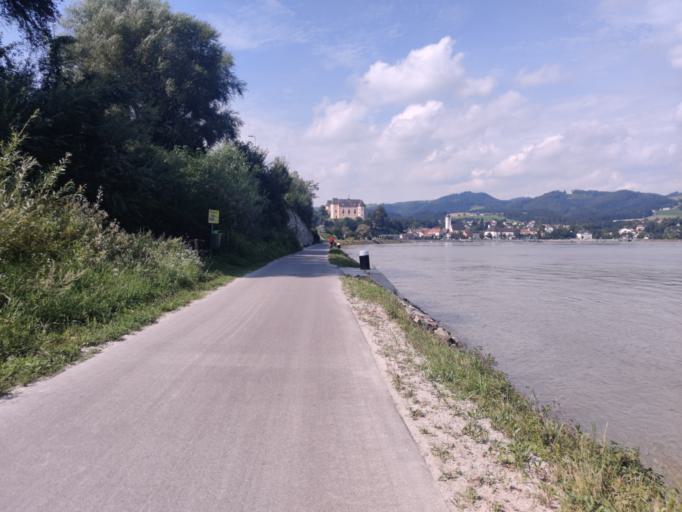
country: AT
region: Upper Austria
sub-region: Politischer Bezirk Perg
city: Bad Kreuzen
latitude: 48.2187
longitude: 14.8552
